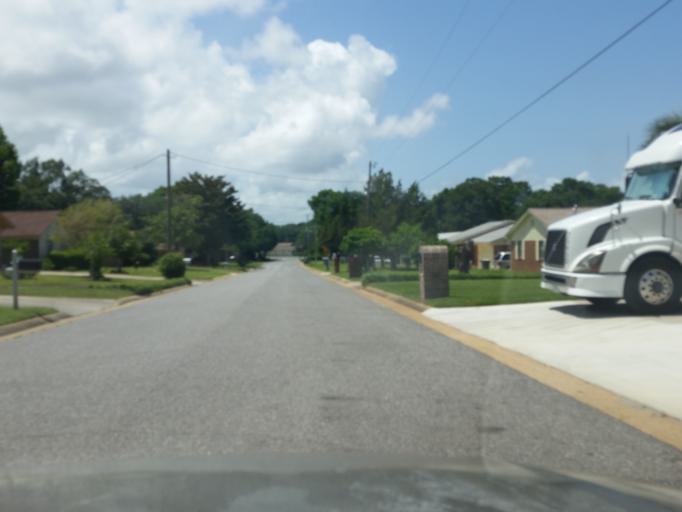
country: US
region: Florida
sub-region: Escambia County
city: Ferry Pass
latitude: 30.5134
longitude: -87.1777
